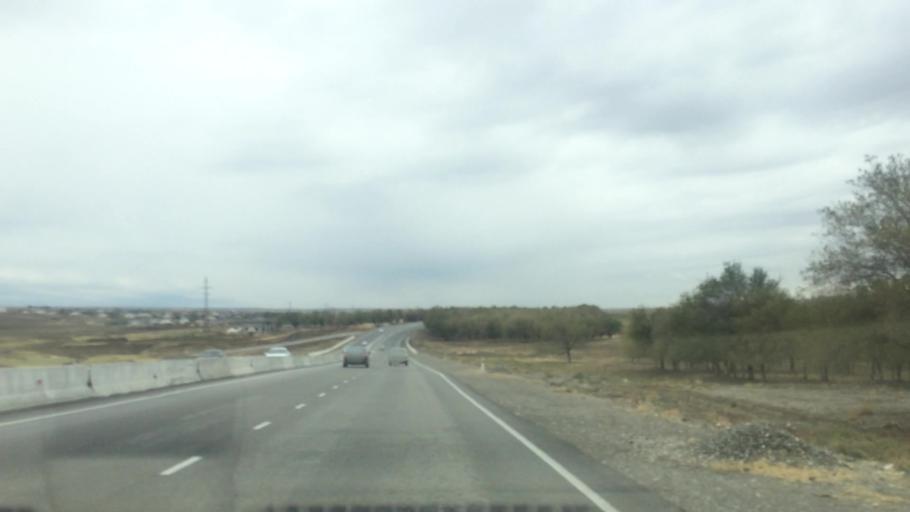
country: UZ
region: Samarqand
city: Bulung'ur
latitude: 39.9223
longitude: 67.5168
